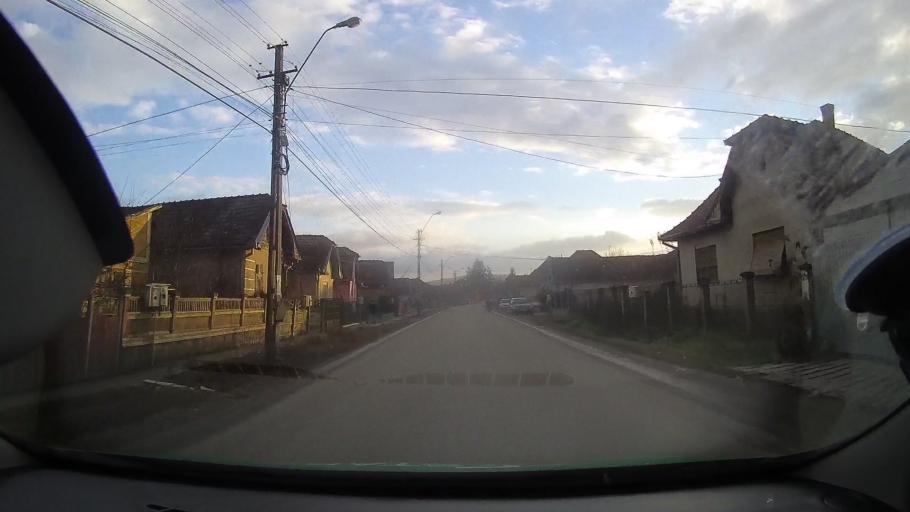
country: RO
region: Alba
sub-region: Oras Ocna Mures
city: Razboieni-Cetate
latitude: 46.4158
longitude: 23.8732
